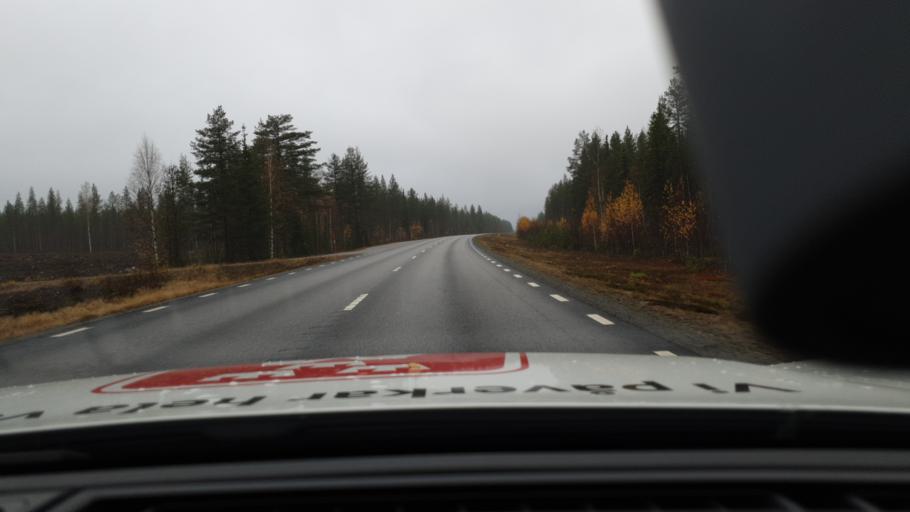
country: SE
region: Norrbotten
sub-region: Overkalix Kommun
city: OEverkalix
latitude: 66.6104
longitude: 22.2433
